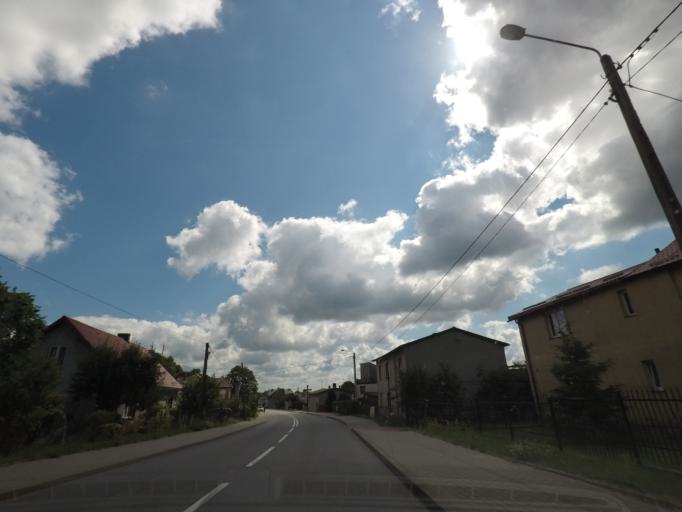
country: PL
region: Pomeranian Voivodeship
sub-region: Powiat wejherowski
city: Leczyce
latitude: 54.5943
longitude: 17.8571
